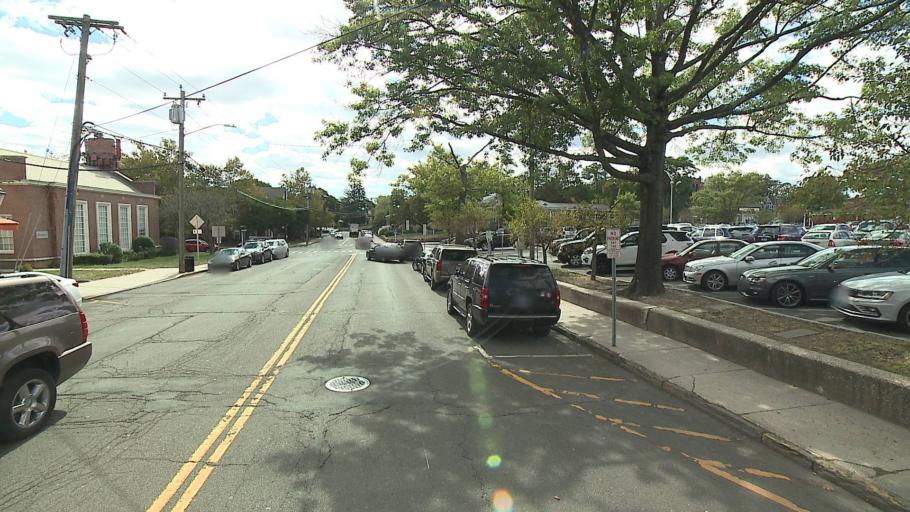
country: US
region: Connecticut
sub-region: Fairfield County
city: New Canaan
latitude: 41.1467
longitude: -73.4921
